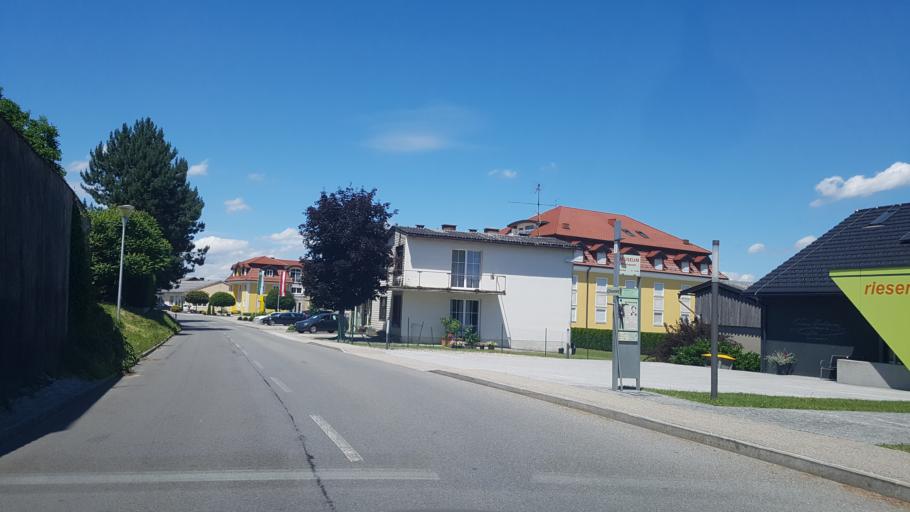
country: AT
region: Salzburg
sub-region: Politischer Bezirk Salzburg-Umgebung
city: Strasswalchen
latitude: 48.0050
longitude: 13.2183
